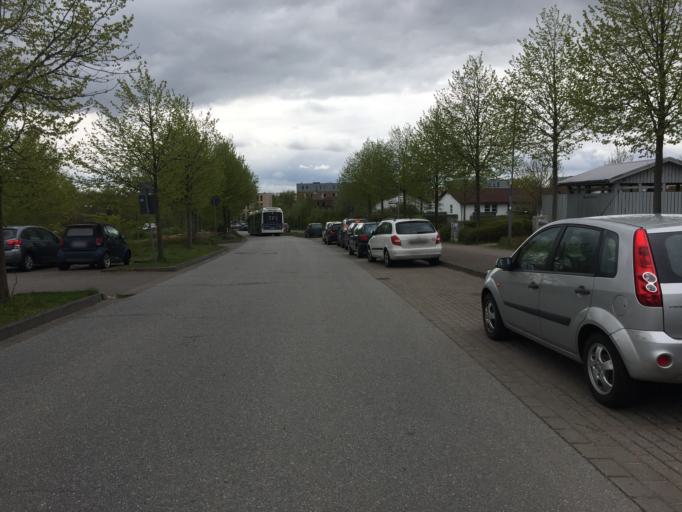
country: DE
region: Schleswig-Holstein
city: Flensburg
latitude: 54.7760
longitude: 9.4494
